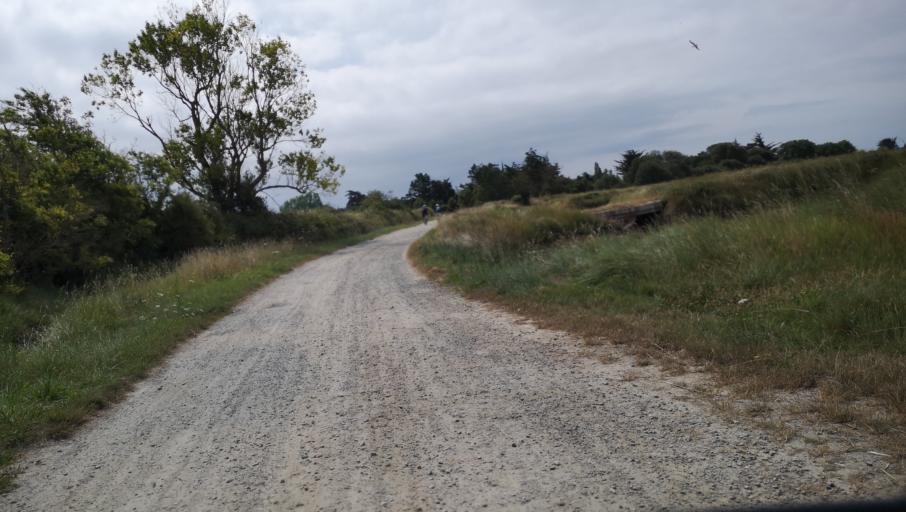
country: FR
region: Pays de la Loire
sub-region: Departement de la Vendee
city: Olonne-sur-Mer
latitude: 46.5671
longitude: -1.7862
